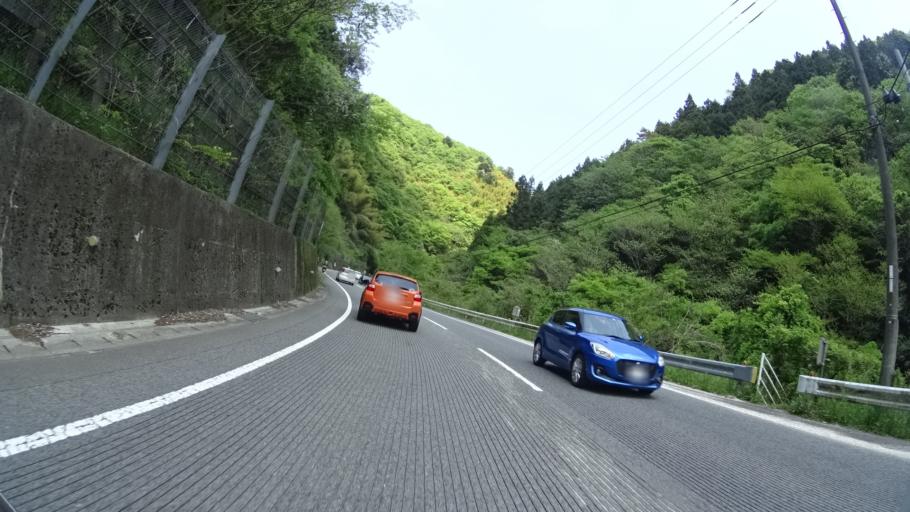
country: JP
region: Ehime
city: Hojo
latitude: 33.9129
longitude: 132.8797
